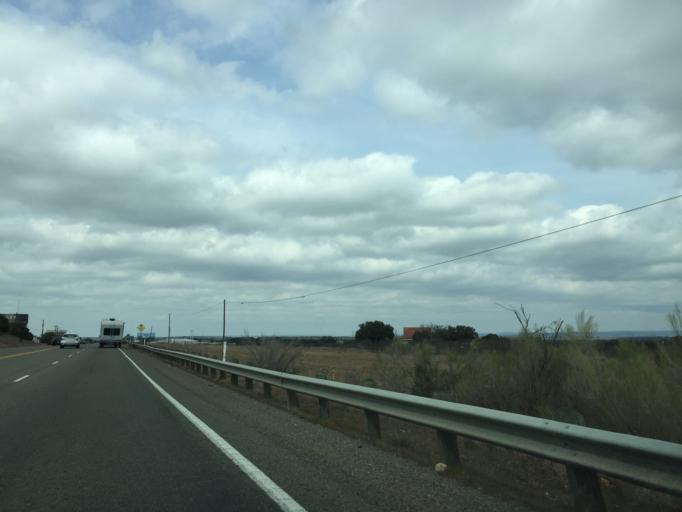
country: US
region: Texas
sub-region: Travis County
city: Briarcliff
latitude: 30.4542
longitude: -98.1503
